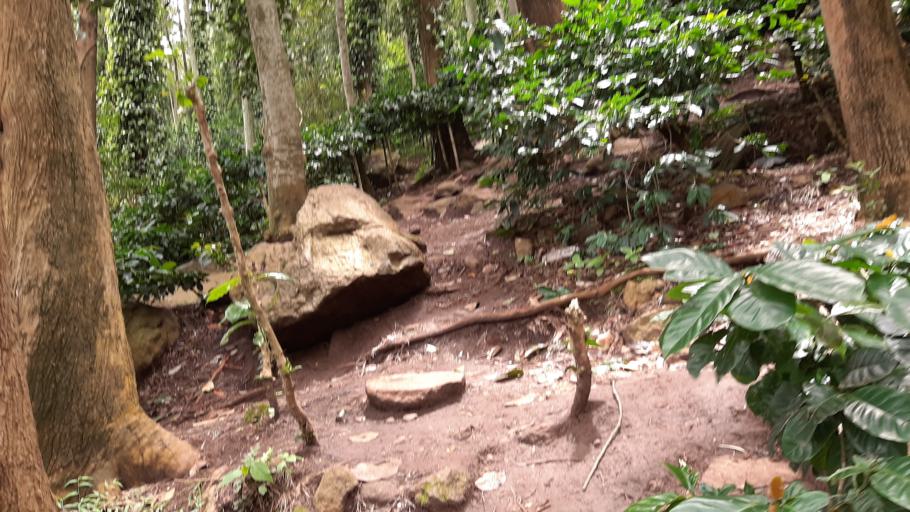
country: IN
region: Andhra Pradesh
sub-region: Vizianagaram District
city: Salur
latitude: 18.2572
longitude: 82.9887
